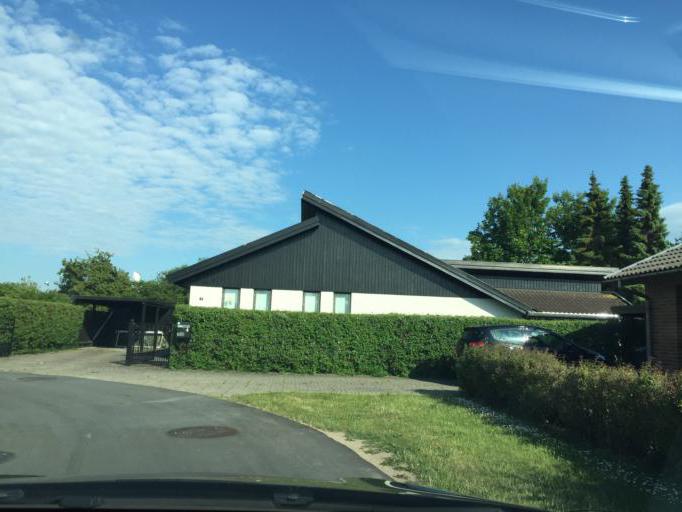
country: DK
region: South Denmark
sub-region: Odense Kommune
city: Neder Holluf
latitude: 55.3708
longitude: 10.4585
